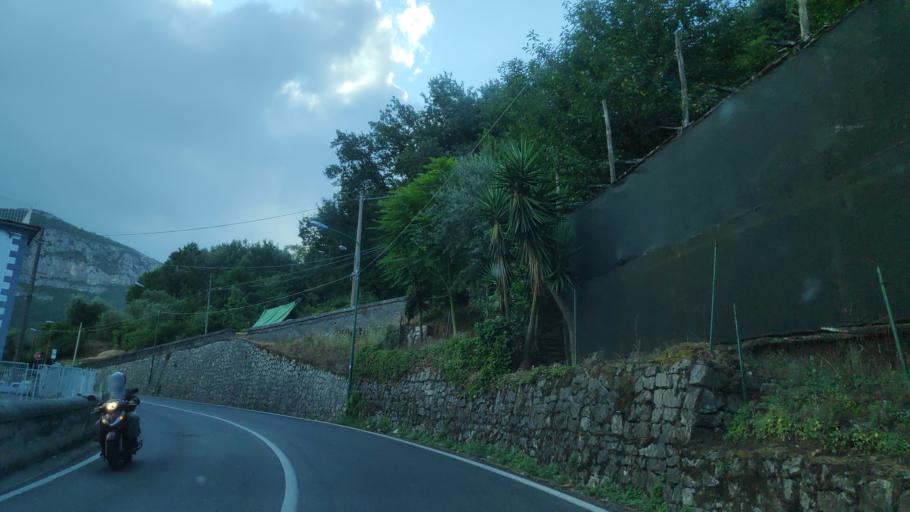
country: IT
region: Campania
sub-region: Provincia di Napoli
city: Piano di Sorrento
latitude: 40.6204
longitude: 14.4174
